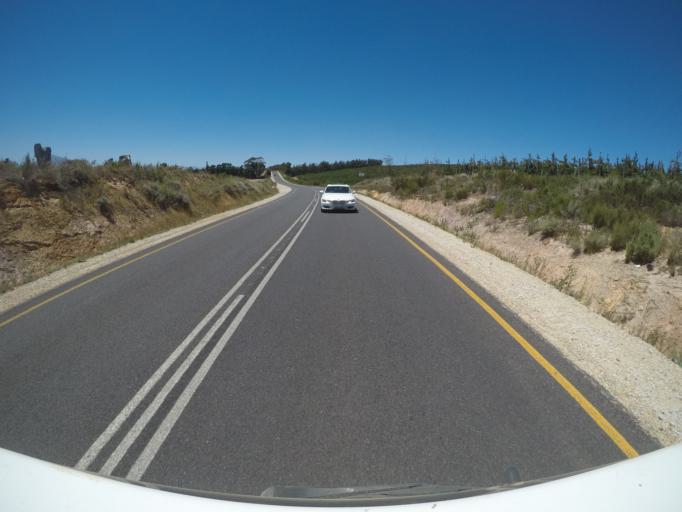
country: ZA
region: Western Cape
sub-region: Overberg District Municipality
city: Grabouw
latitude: -34.0680
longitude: 19.1228
